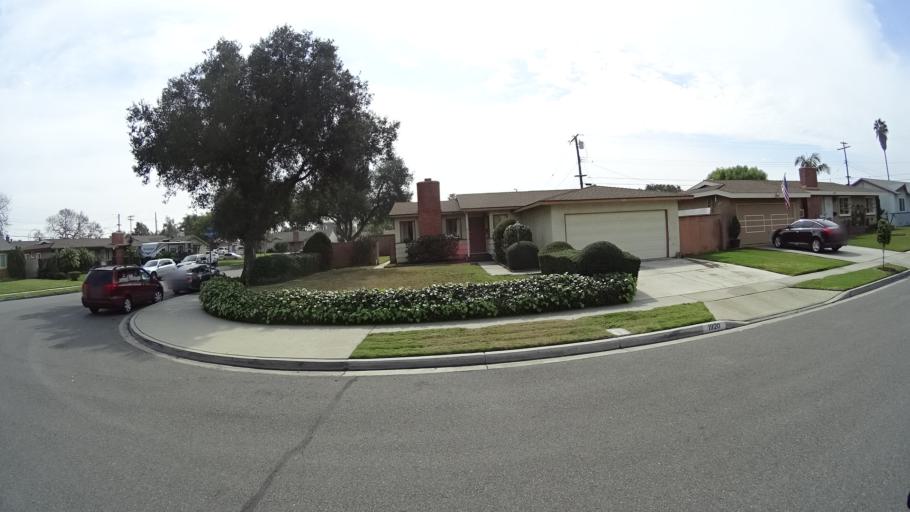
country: US
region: California
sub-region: Orange County
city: Garden Grove
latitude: 33.8113
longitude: -117.9512
